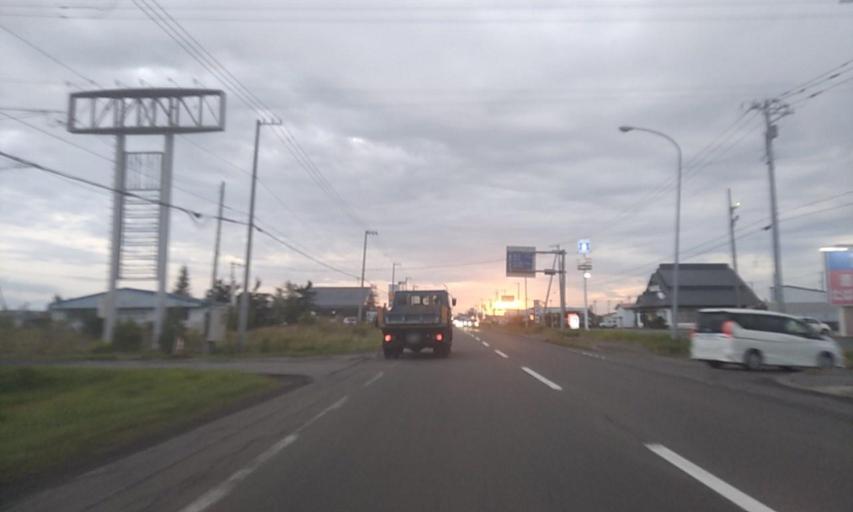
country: JP
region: Hokkaido
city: Abashiri
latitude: 43.9005
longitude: 144.6568
